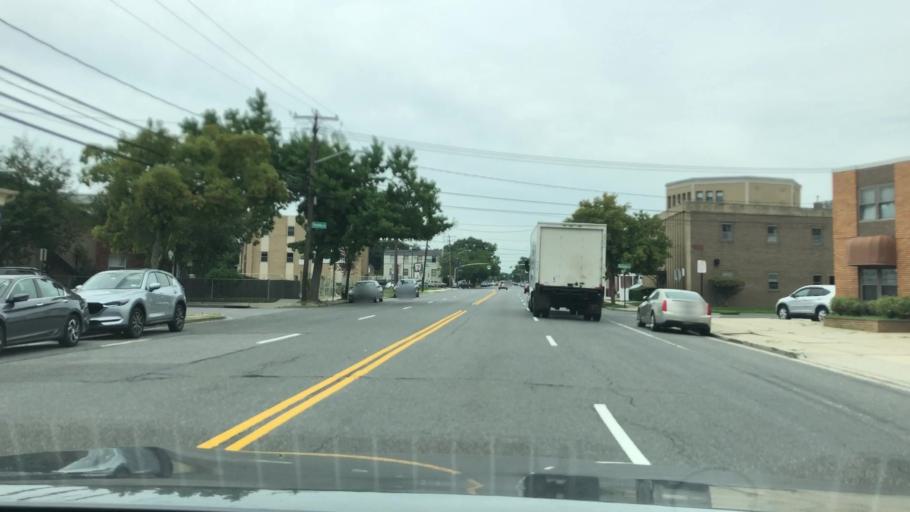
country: US
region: New York
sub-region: Nassau County
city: North Massapequa
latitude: 40.6907
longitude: -73.4657
